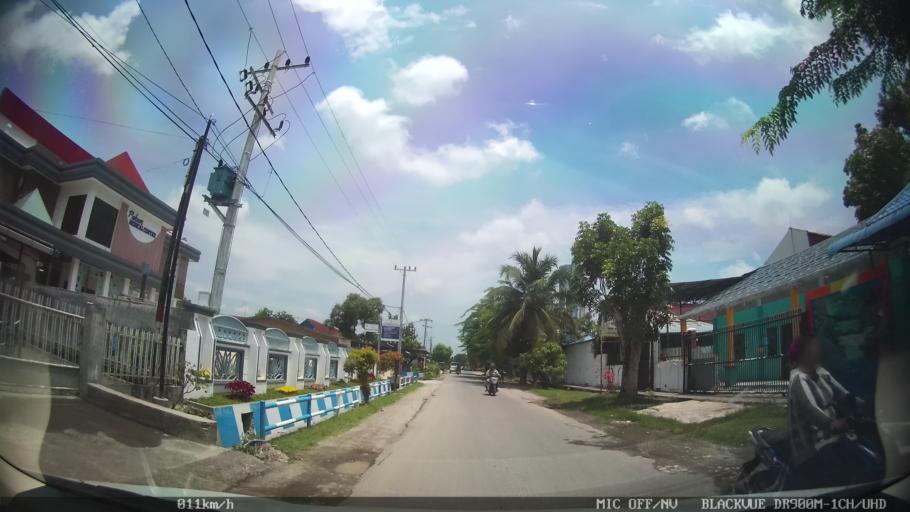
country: ID
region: North Sumatra
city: Perbaungan
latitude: 3.5416
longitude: 98.8793
